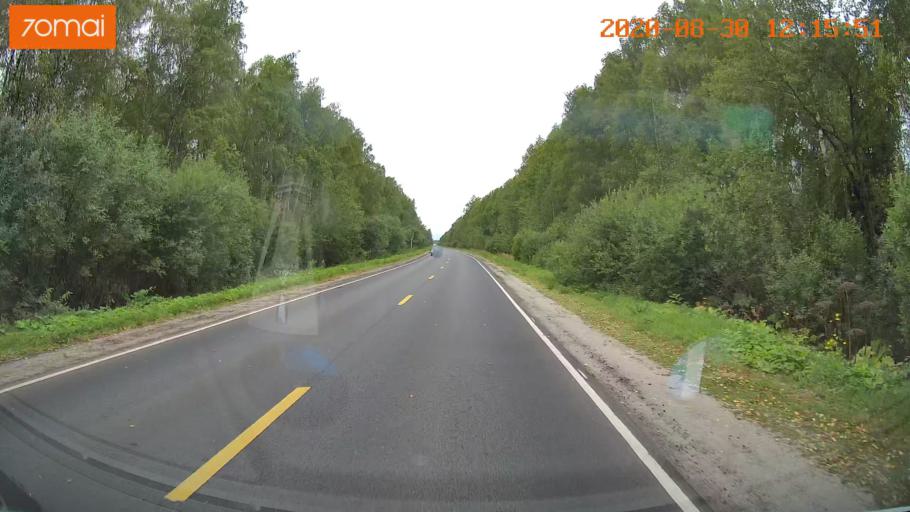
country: RU
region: Ivanovo
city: Yur'yevets
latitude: 57.3187
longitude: 43.0191
